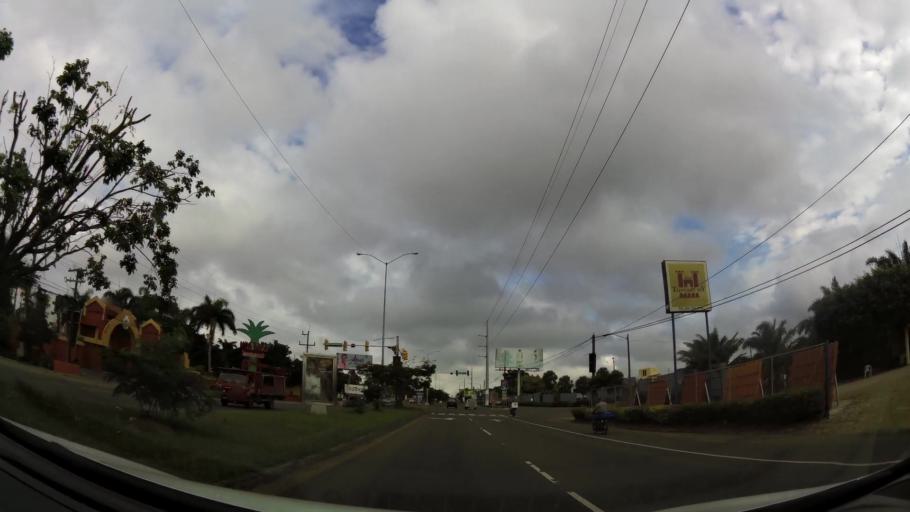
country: DO
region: Santiago
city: Licey al Medio
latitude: 19.4204
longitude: -70.6481
